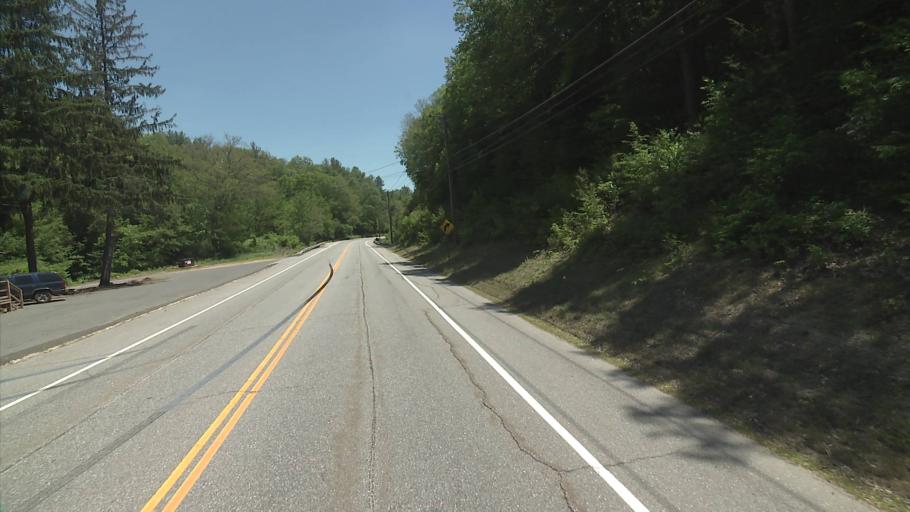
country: US
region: Connecticut
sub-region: Tolland County
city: Stafford
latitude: 41.9934
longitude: -72.2720
